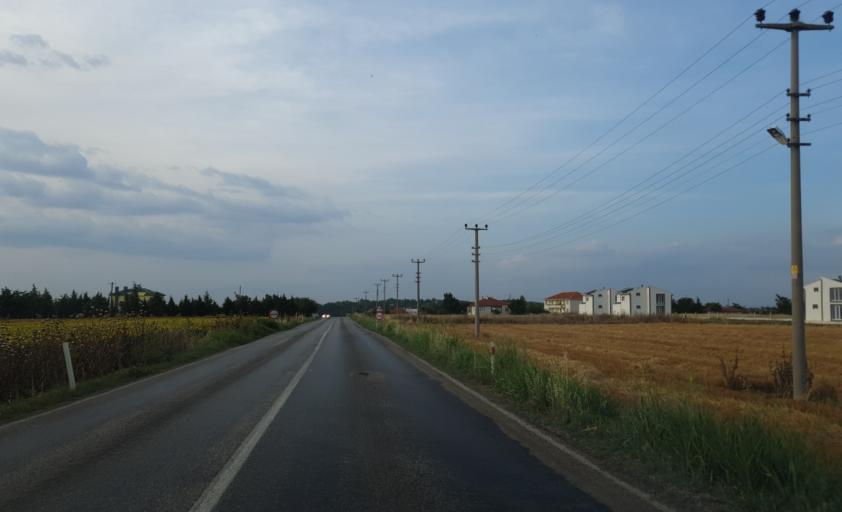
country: TR
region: Kirklareli
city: Babaeski
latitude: 41.3497
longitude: 27.1426
